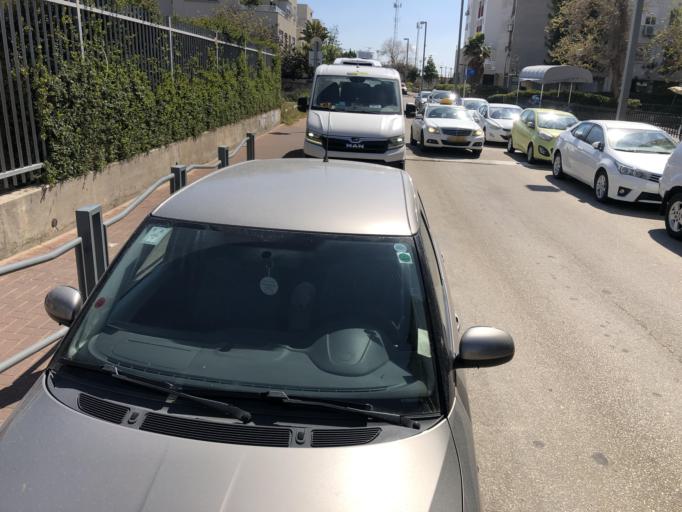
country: IL
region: Tel Aviv
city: Bat Yam
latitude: 32.0075
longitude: 34.7600
